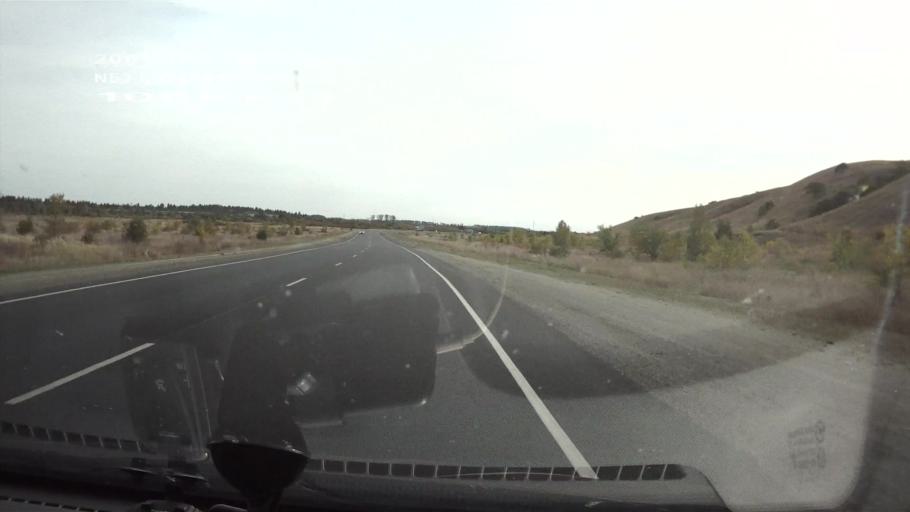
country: RU
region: Saratov
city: Sennoy
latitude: 52.0969
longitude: 46.8130
